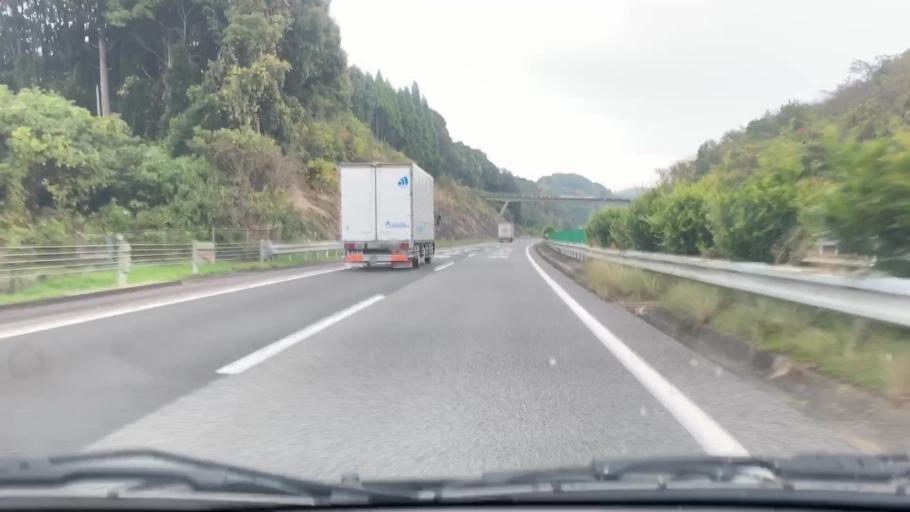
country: JP
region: Saga Prefecture
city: Takeocho-takeo
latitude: 33.2290
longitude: 130.0526
